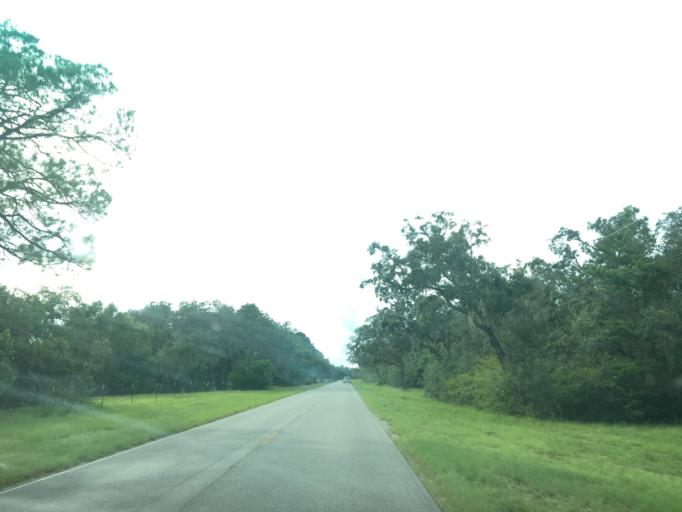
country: US
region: Florida
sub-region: Wakulla County
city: Crawfordville
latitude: 29.9090
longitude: -84.3601
